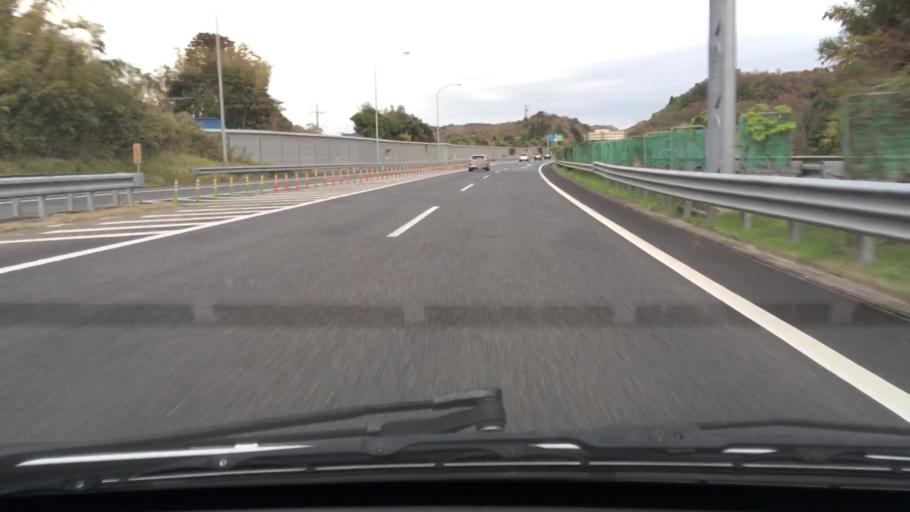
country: JP
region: Chiba
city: Kisarazu
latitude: 35.3806
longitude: 139.9855
